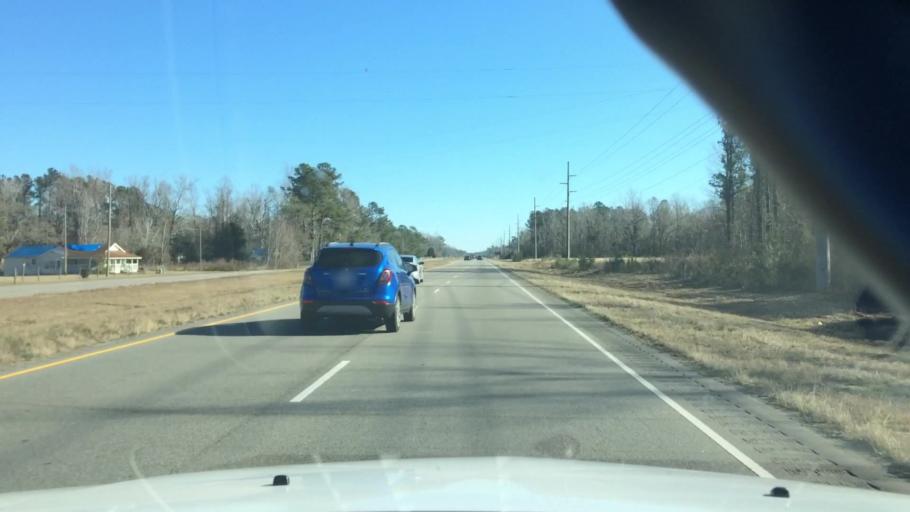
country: US
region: North Carolina
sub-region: Brunswick County
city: Shallotte
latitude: 34.0033
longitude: -78.3124
